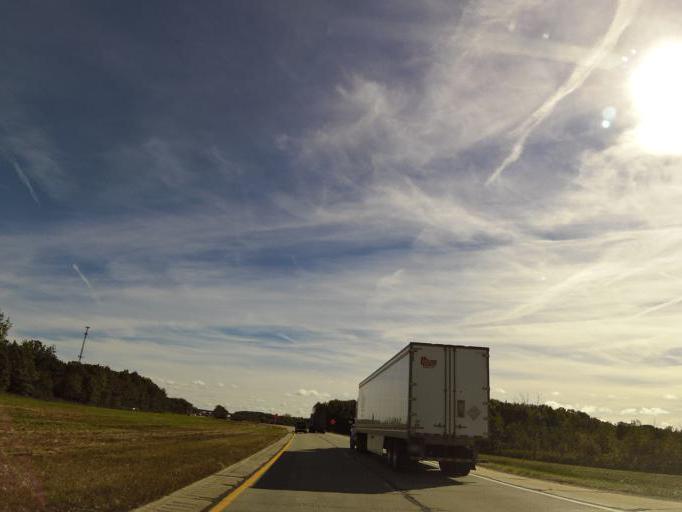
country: US
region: Michigan
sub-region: Saint Clair County
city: Capac
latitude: 42.9765
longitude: -82.8324
